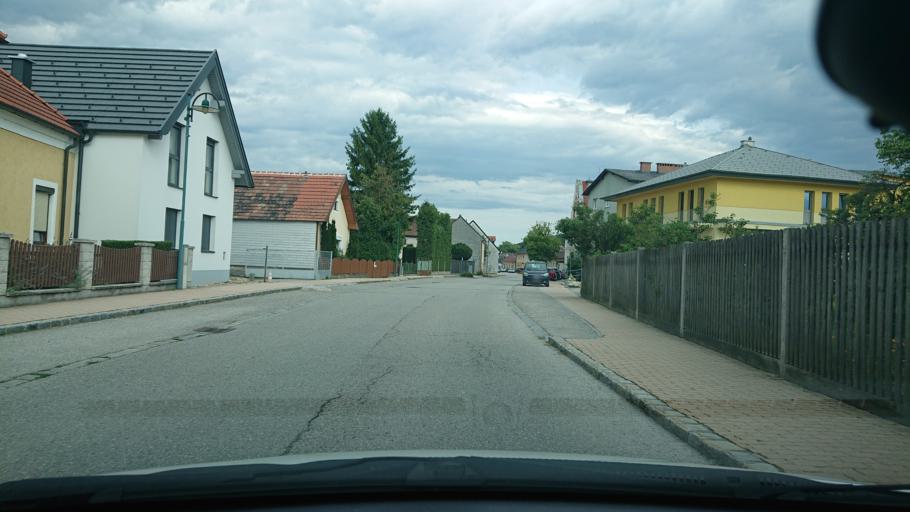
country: AT
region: Lower Austria
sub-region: Politischer Bezirk Baden
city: Hirtenberg
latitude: 47.9385
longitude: 16.1493
